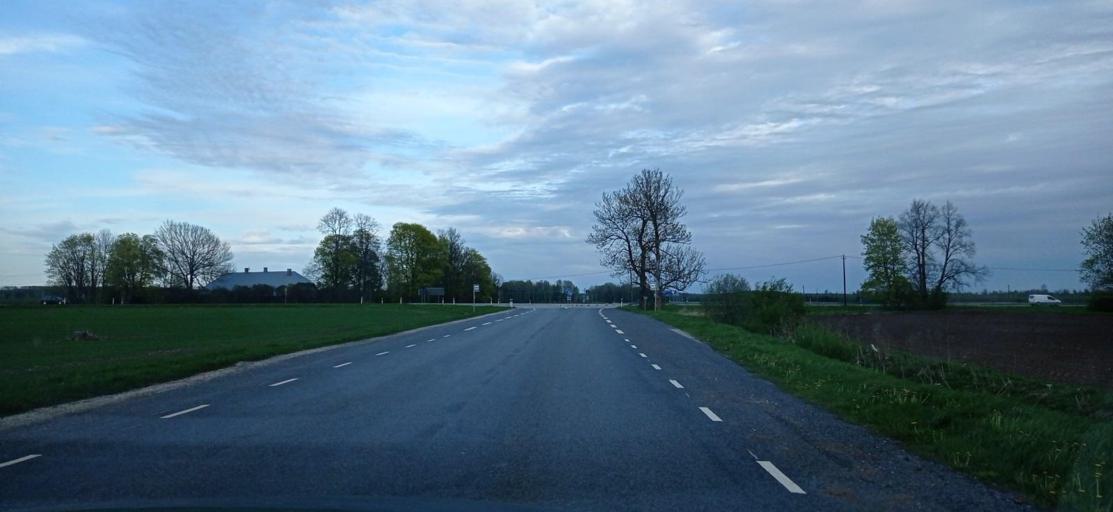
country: EE
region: Paernumaa
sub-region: Tootsi vald
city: Tootsi
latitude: 58.5543
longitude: 24.8524
